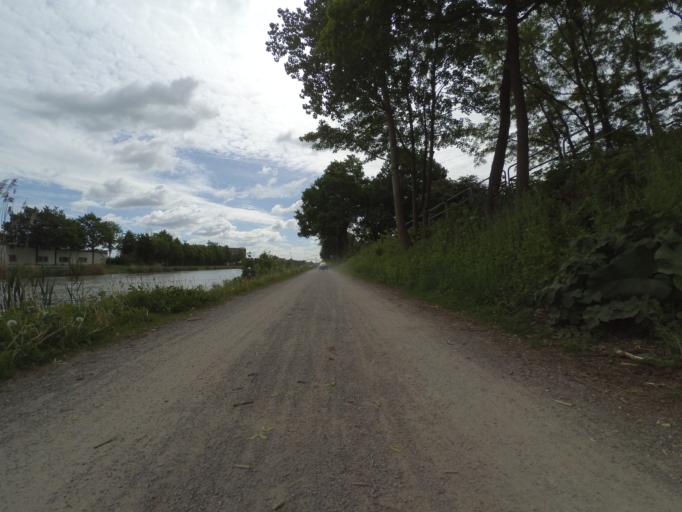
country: DE
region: Lower Saxony
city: Langenhagen
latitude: 52.4187
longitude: 9.7072
